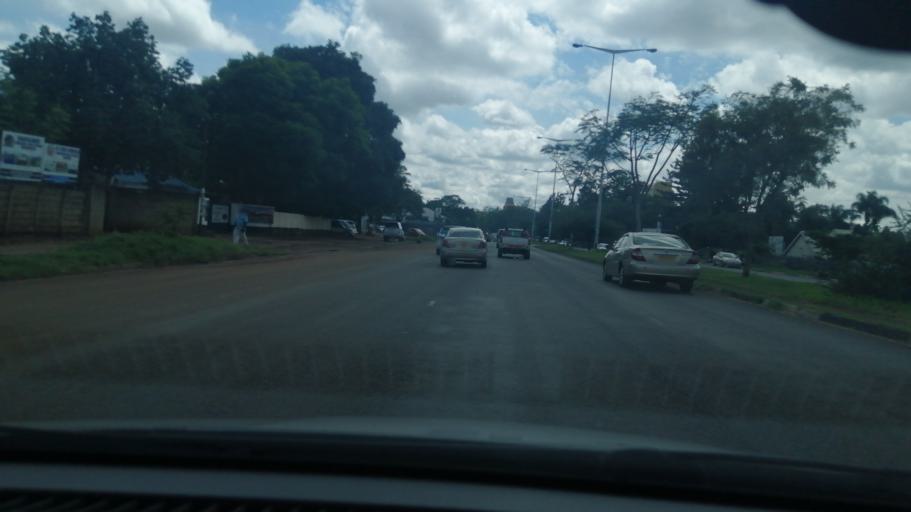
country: ZW
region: Harare
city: Harare
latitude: -17.8290
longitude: 31.0275
